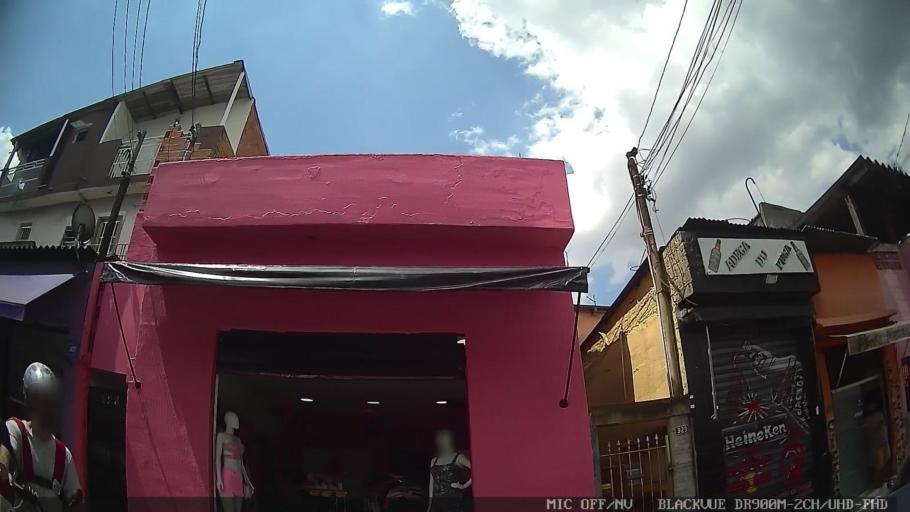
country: BR
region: Sao Paulo
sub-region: Ferraz De Vasconcelos
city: Ferraz de Vasconcelos
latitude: -23.5559
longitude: -46.4522
